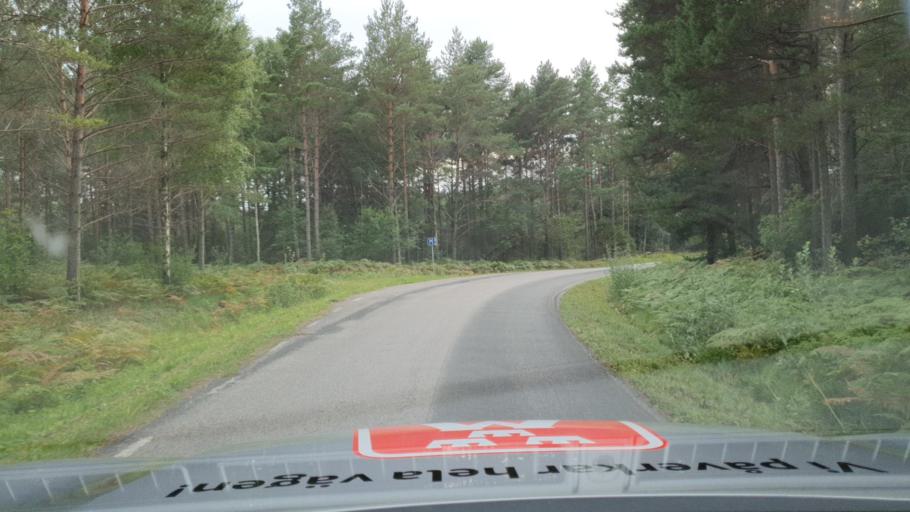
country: SE
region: Gotland
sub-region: Gotland
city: Vibble
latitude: 57.5031
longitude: 18.2595
